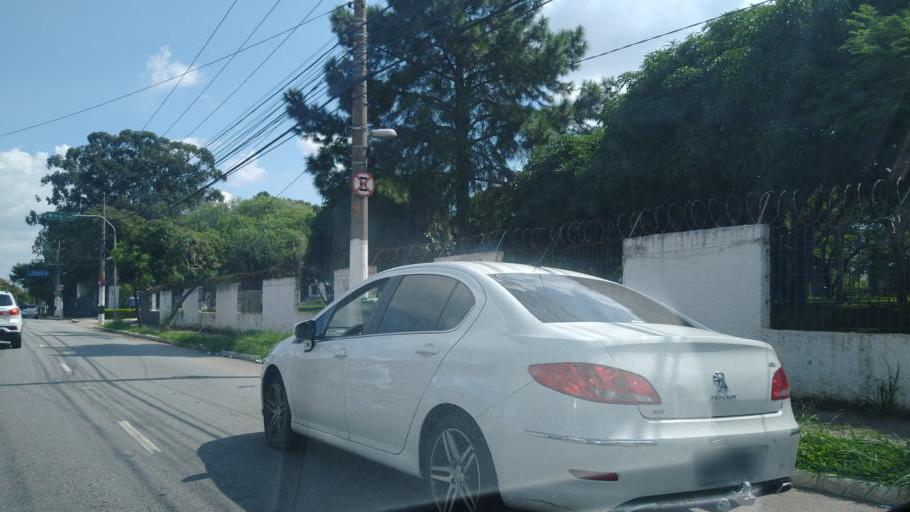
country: BR
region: Sao Paulo
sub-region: Sao Paulo
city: Sao Paulo
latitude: -23.5152
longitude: -46.6423
